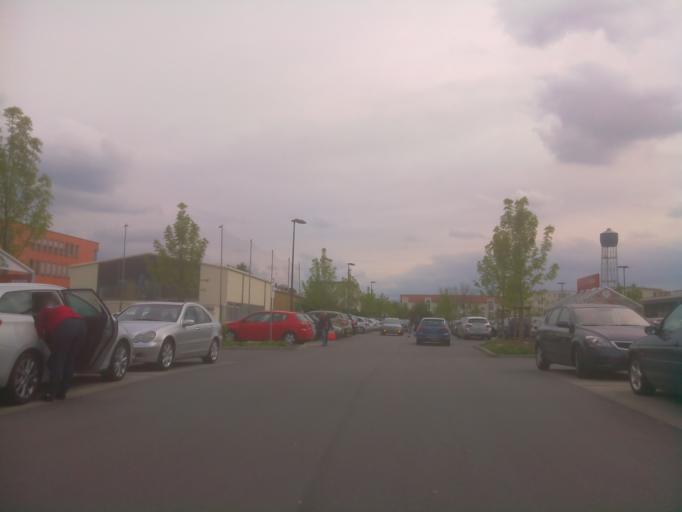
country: DE
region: Baden-Wuerttemberg
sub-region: Karlsruhe Region
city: Heidelberg
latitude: 49.3842
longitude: 8.6795
